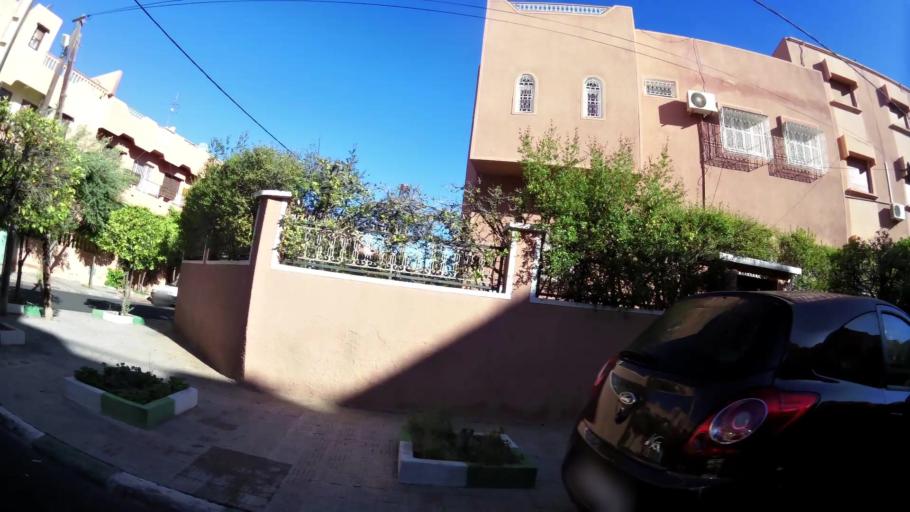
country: MA
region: Marrakech-Tensift-Al Haouz
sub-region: Marrakech
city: Marrakesh
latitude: 31.6486
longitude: -8.0185
